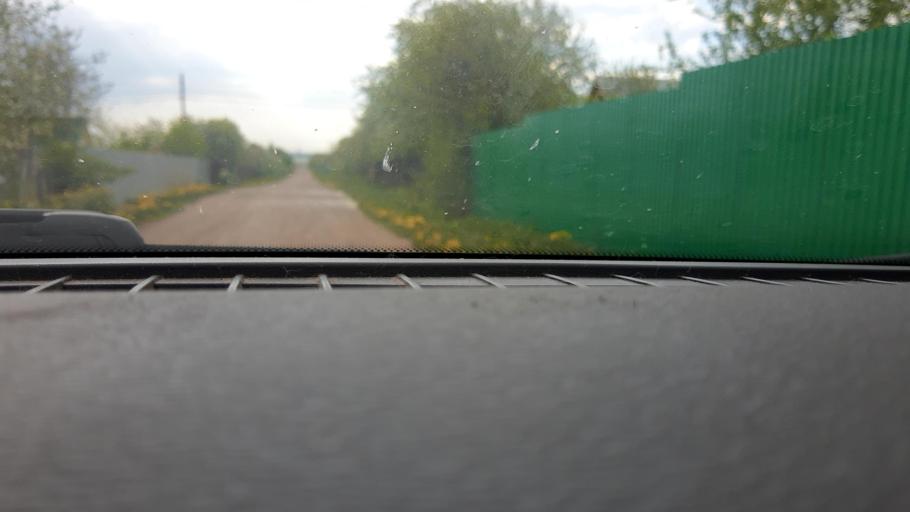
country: RU
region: Bashkortostan
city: Avdon
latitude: 54.5682
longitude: 55.7419
